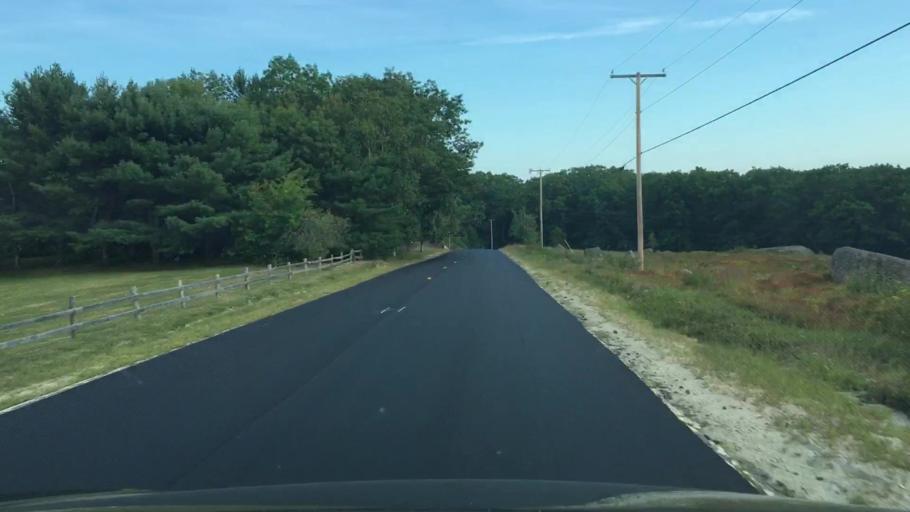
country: US
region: Maine
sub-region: Hancock County
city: Surry
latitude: 44.5273
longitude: -68.6106
